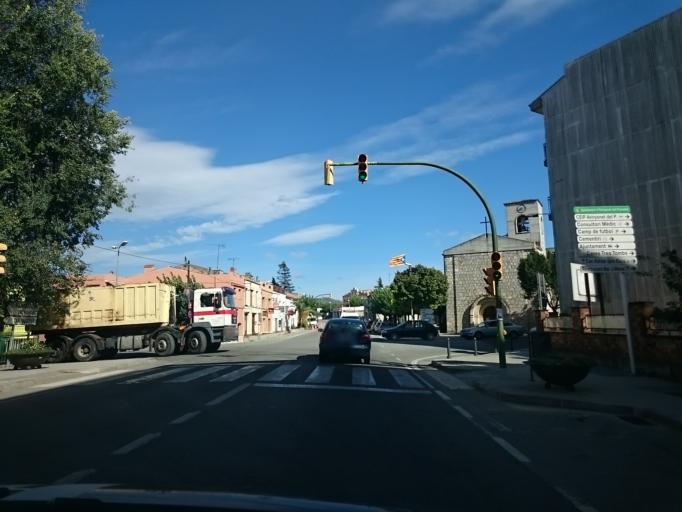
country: ES
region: Catalonia
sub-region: Provincia de Barcelona
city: Avinyonet del Penedes
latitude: 41.3613
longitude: 1.7762
